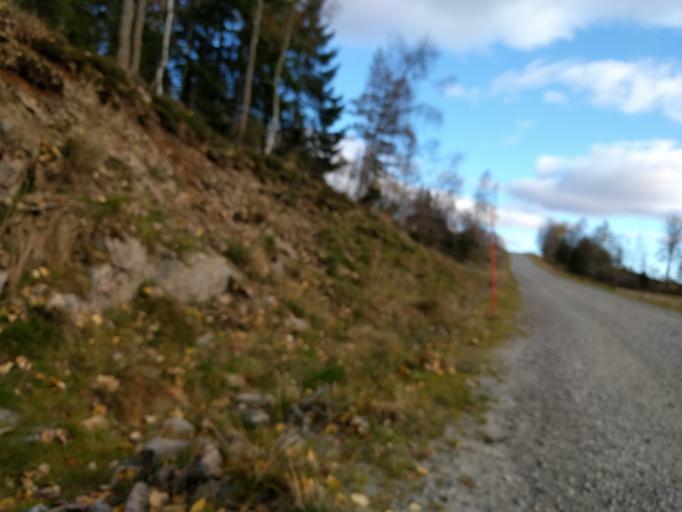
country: NO
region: Aust-Agder
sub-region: Evje og Hornnes
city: Evje
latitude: 58.6538
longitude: 7.9458
